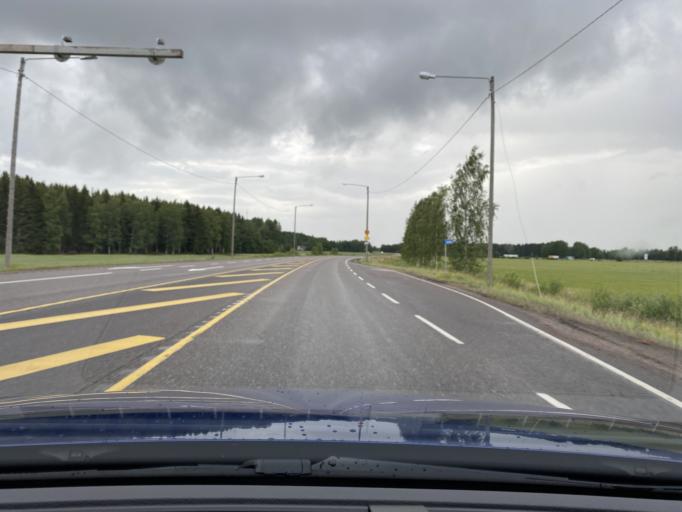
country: FI
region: Uusimaa
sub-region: Helsinki
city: Hyvinge
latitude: 60.5783
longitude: 24.7965
